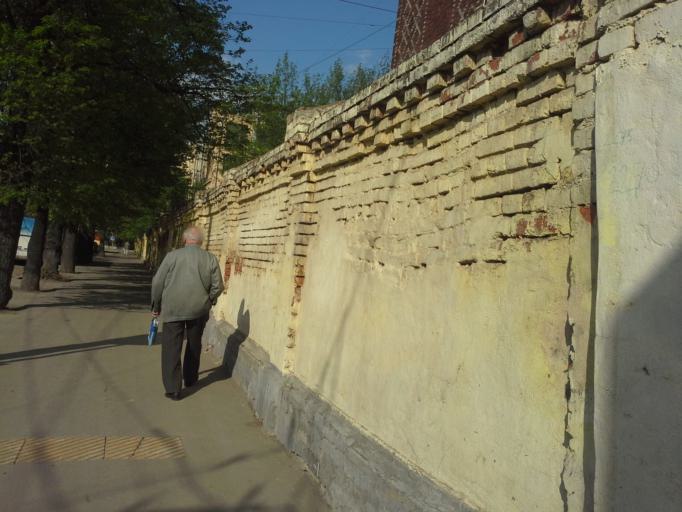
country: RU
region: Moscow
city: Mar'ina Roshcha
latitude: 55.7793
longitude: 37.5931
